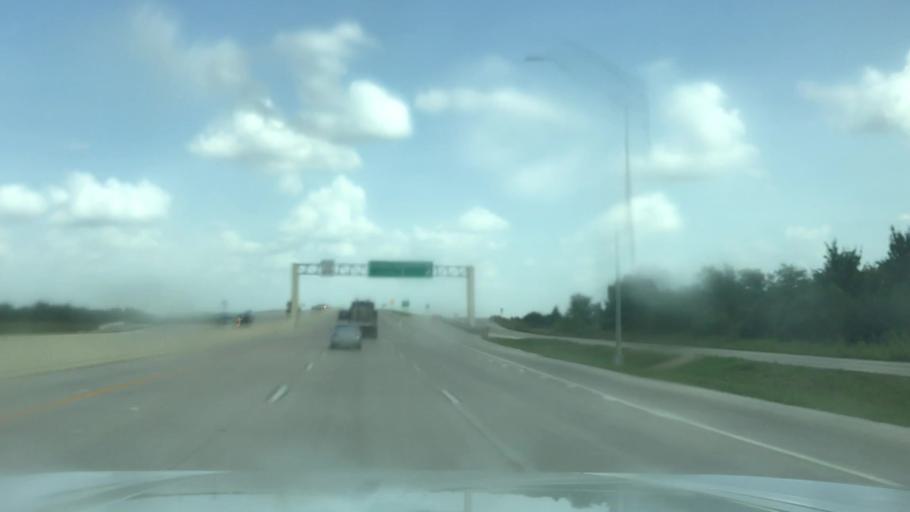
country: US
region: Texas
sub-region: Waller County
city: Waller
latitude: 30.0591
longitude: -95.8964
